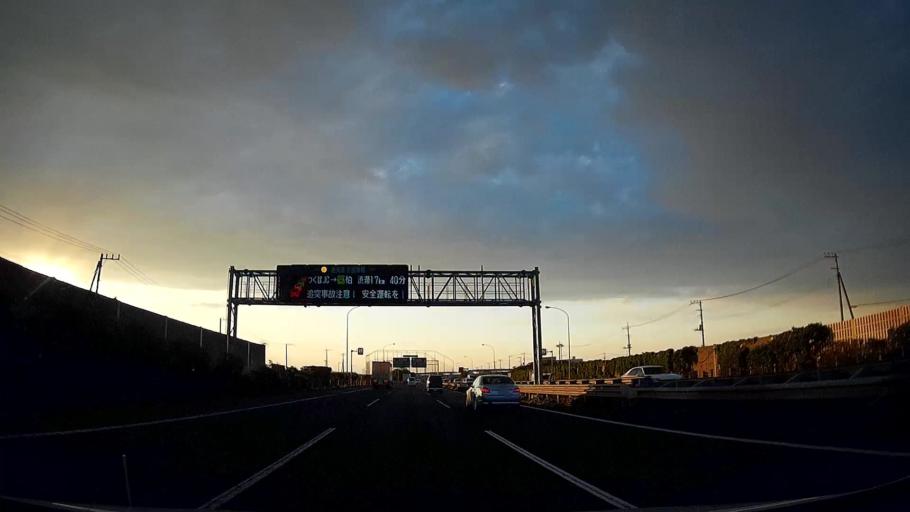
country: JP
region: Saitama
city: Shiraoka
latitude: 36.0378
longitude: 139.6630
